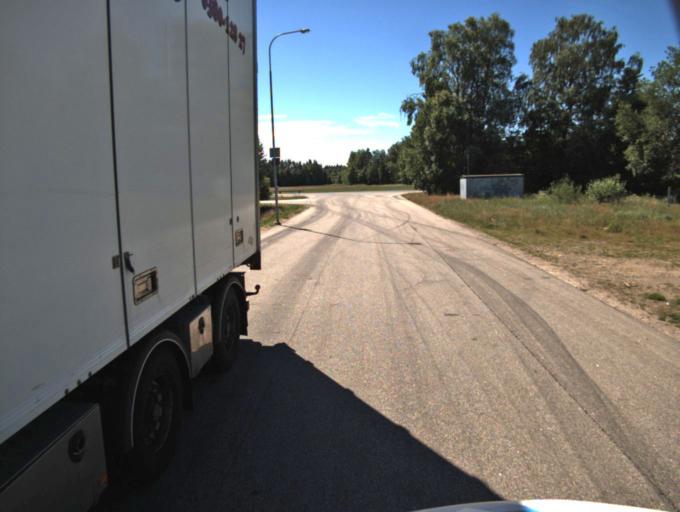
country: SE
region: Vaestra Goetaland
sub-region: Ulricehamns Kommun
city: Ulricehamn
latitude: 57.6699
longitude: 13.4364
